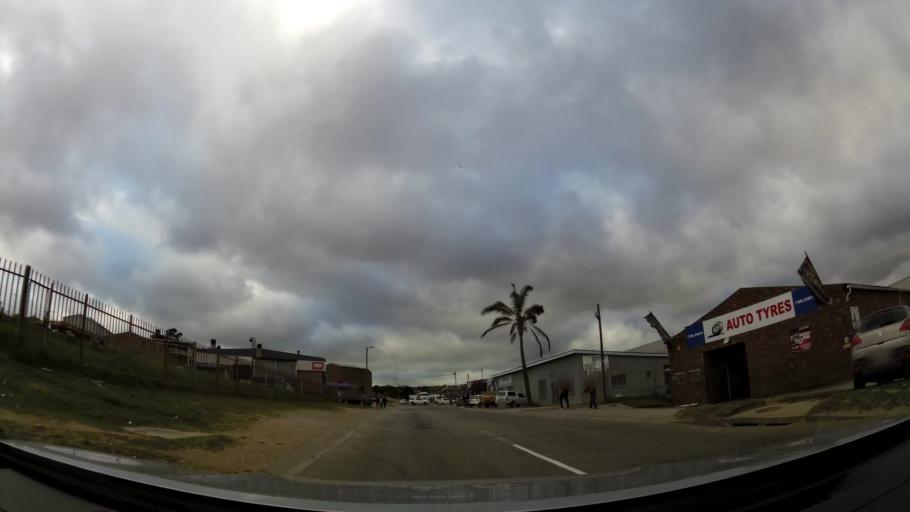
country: ZA
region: Western Cape
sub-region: Eden District Municipality
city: Plettenberg Bay
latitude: -34.0495
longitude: 23.3558
